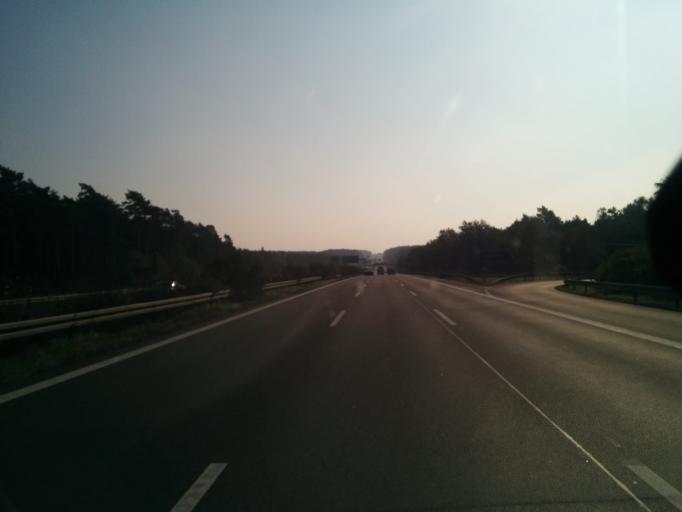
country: DE
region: Brandenburg
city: Fichtenwalde
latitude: 52.3097
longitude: 12.8769
